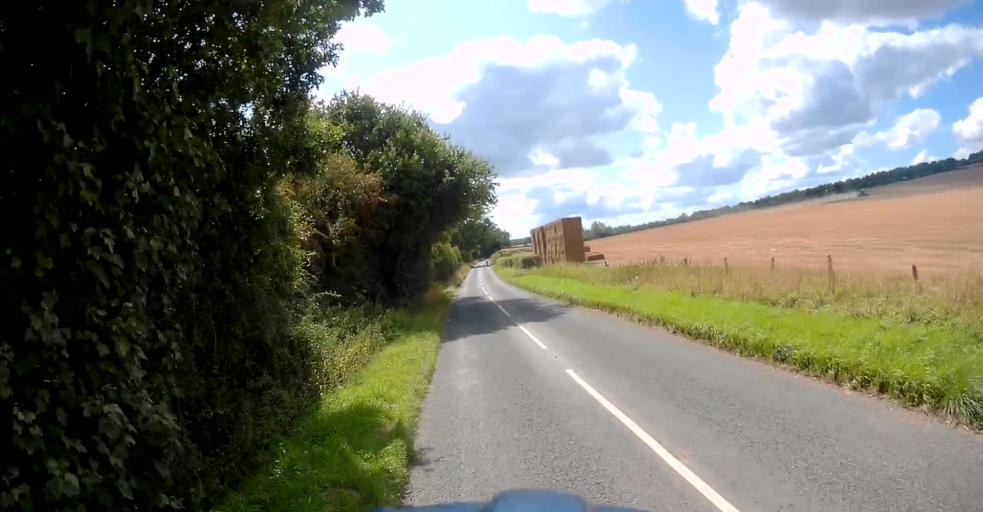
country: GB
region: England
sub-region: Hampshire
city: Four Marks
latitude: 51.1660
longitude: -1.1400
